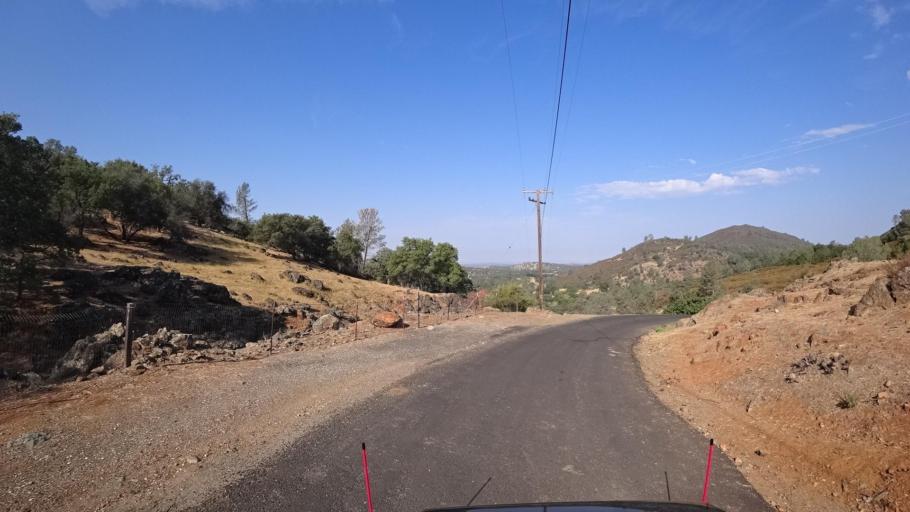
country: US
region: California
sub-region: Tuolumne County
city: Tuolumne City
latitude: 37.7234
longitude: -120.2633
